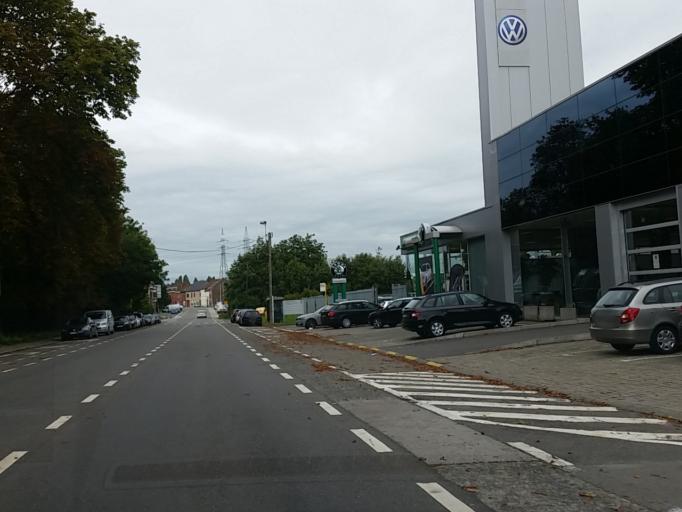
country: BE
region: Flanders
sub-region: Provincie Vlaams-Brabant
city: Machelen
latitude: 50.9219
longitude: 4.4523
